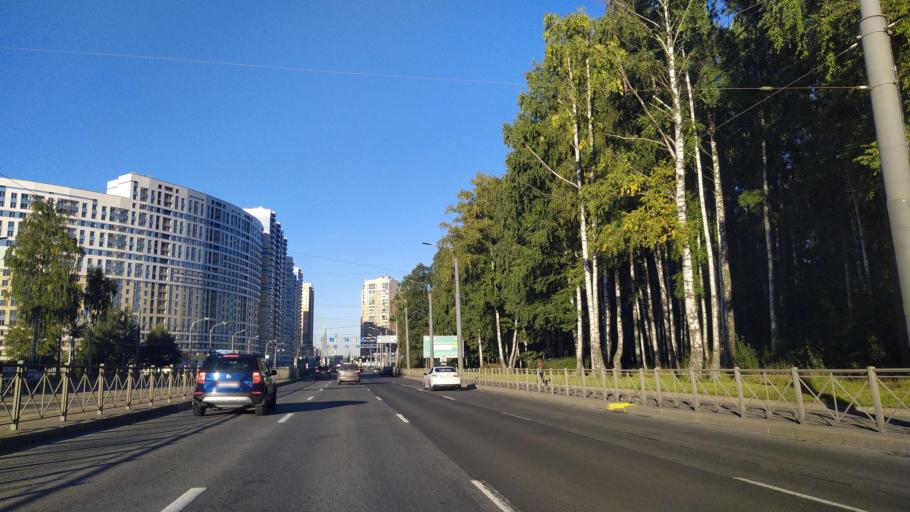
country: RU
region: Leningrad
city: Udel'naya
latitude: 60.0024
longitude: 30.3127
